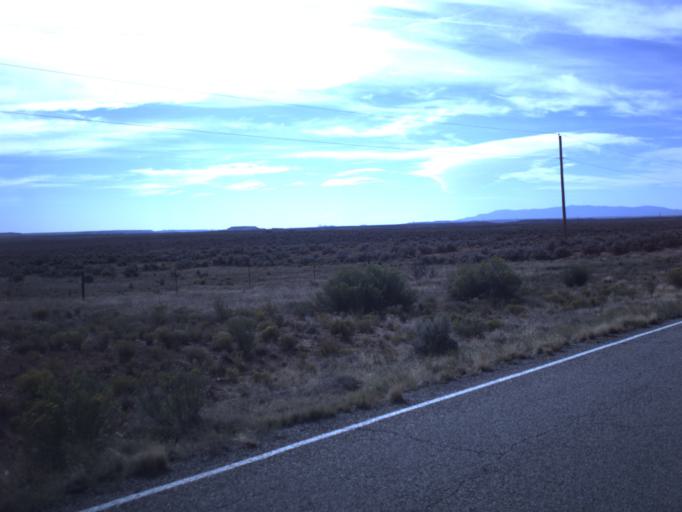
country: US
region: Utah
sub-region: San Juan County
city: Blanding
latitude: 37.4026
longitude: -109.3371
